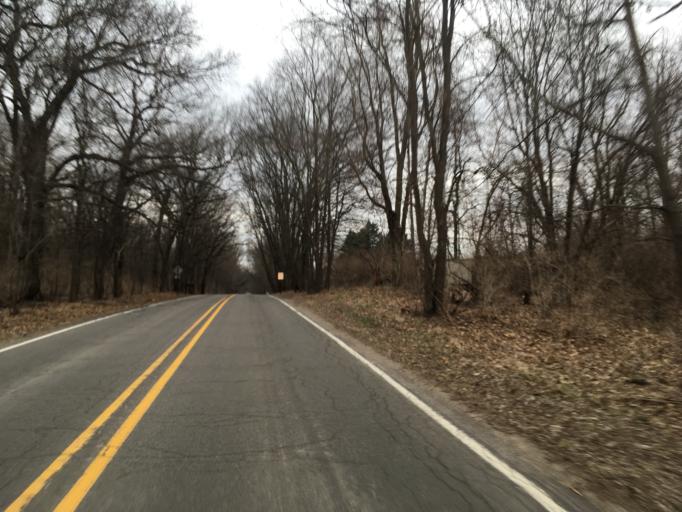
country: US
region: Michigan
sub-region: Washtenaw County
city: Chelsea
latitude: 42.3537
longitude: -84.1195
